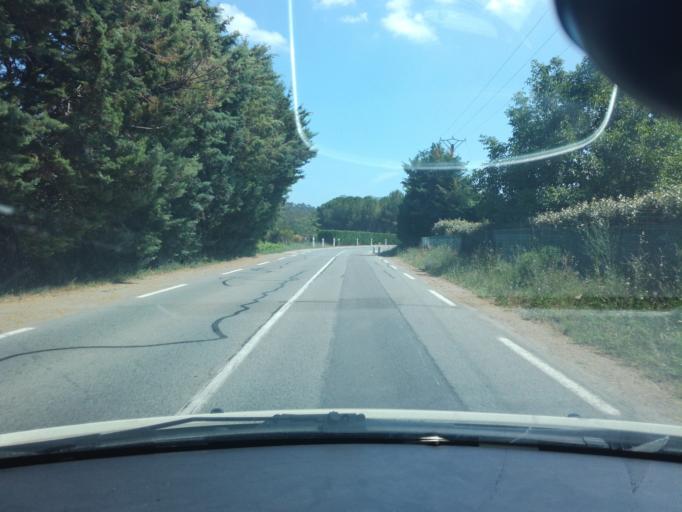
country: FR
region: Provence-Alpes-Cote d'Azur
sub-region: Departement du Var
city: Le Muy
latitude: 43.4872
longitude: 6.5666
